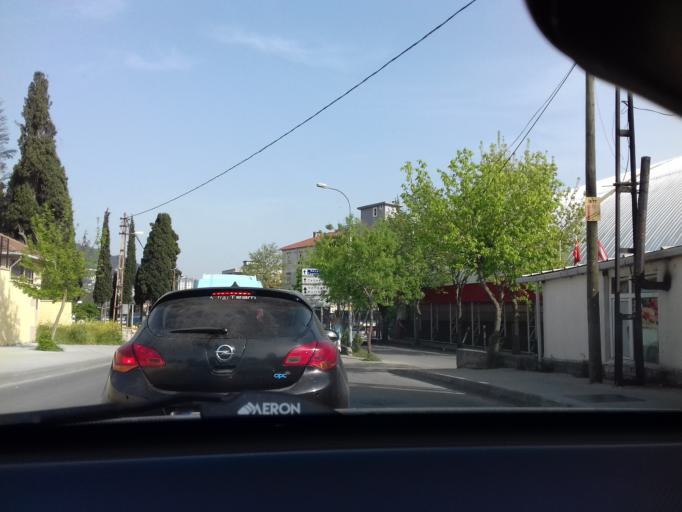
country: TR
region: Istanbul
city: Pendik
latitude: 40.9151
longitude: 29.2221
